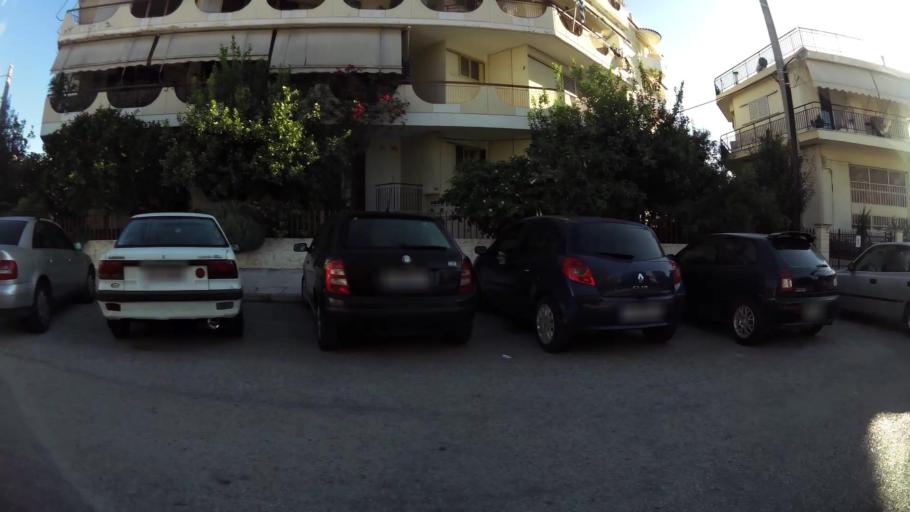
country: GR
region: Attica
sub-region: Nomarchia Anatolikis Attikis
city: Pallini
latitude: 37.9988
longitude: 23.8759
